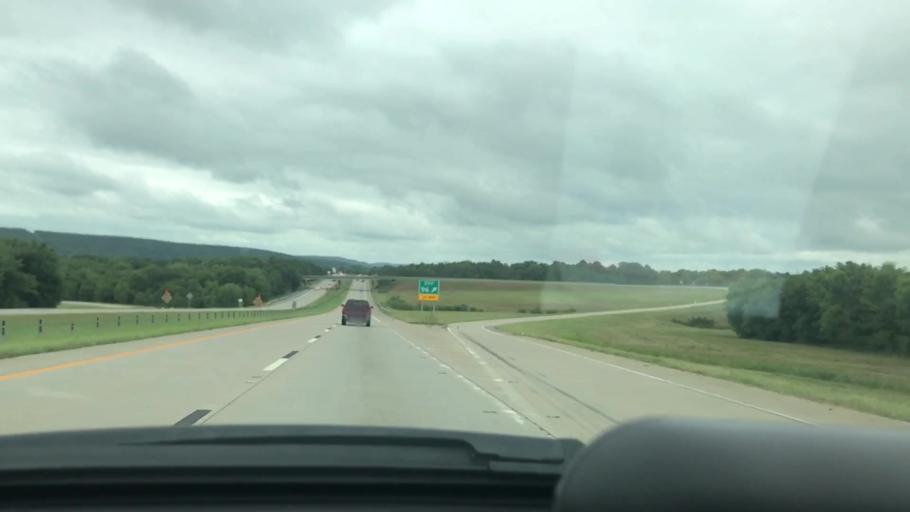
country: US
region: Oklahoma
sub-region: Pittsburg County
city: Krebs
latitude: 34.9959
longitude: -95.7208
